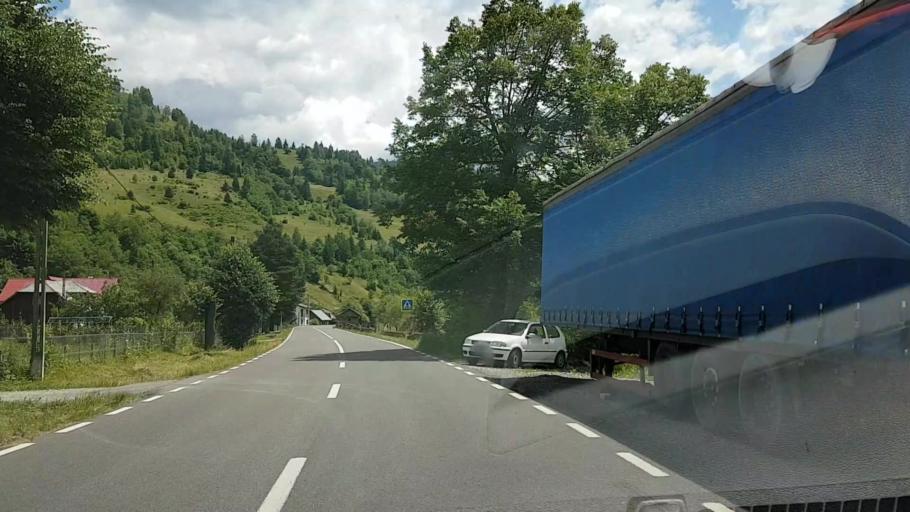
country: RO
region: Suceava
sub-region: Comuna Crucea
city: Crucea
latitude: 47.3916
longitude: 25.5753
